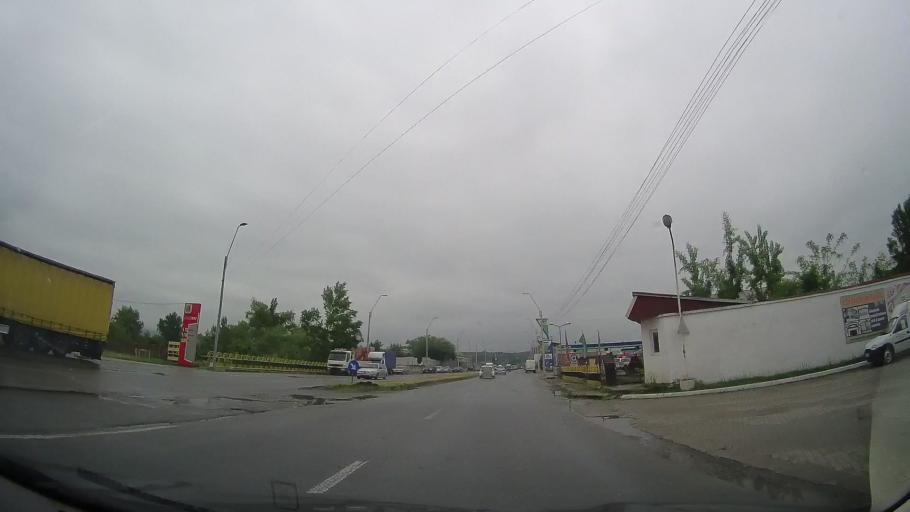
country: RO
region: Mehedinti
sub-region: Comuna Simian
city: Dudasu
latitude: 44.6311
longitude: 22.6850
